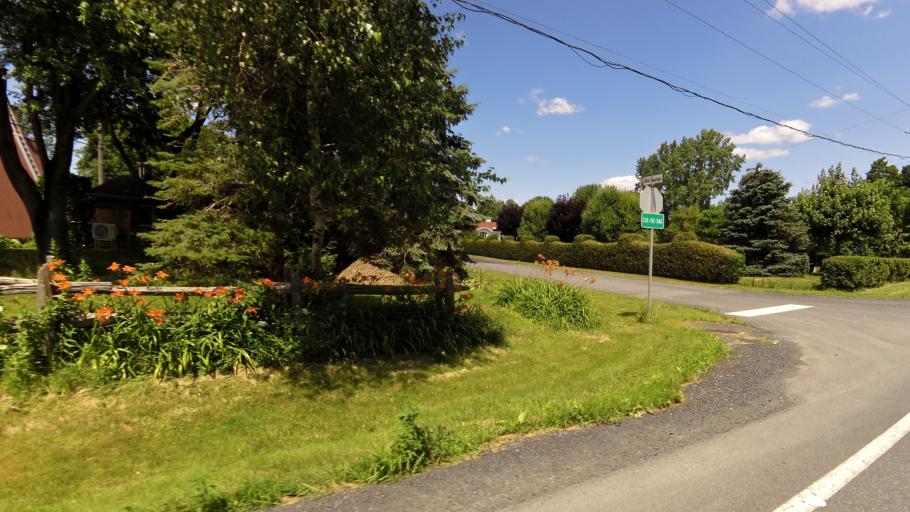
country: CA
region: Quebec
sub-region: Monteregie
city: Saint-Jean-sur-Richelieu
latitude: 45.3627
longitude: -73.2457
